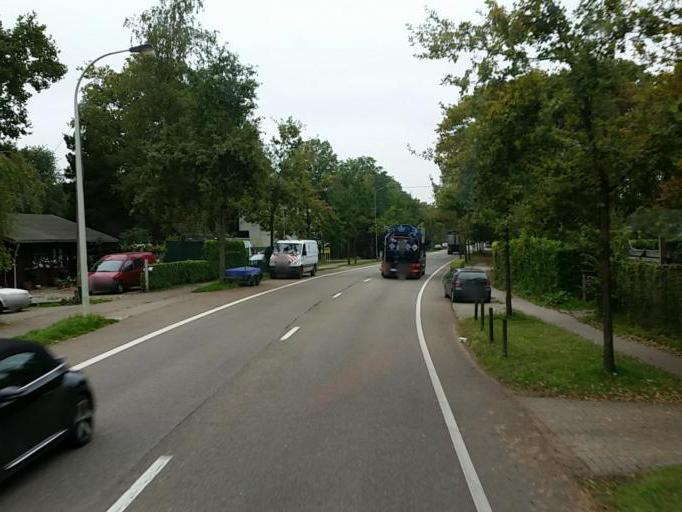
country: BE
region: Flanders
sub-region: Provincie Antwerpen
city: Schoten
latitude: 51.2751
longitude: 4.5235
